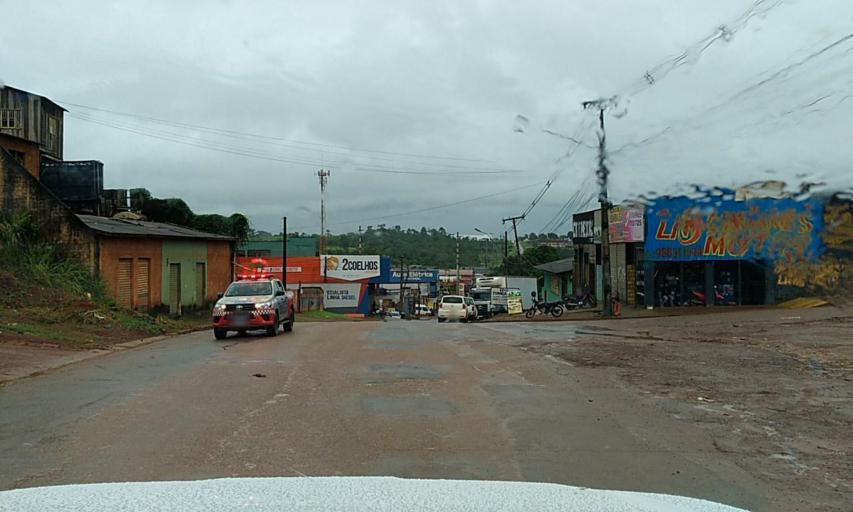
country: BR
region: Para
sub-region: Altamira
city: Altamira
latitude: -3.2144
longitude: -52.2358
